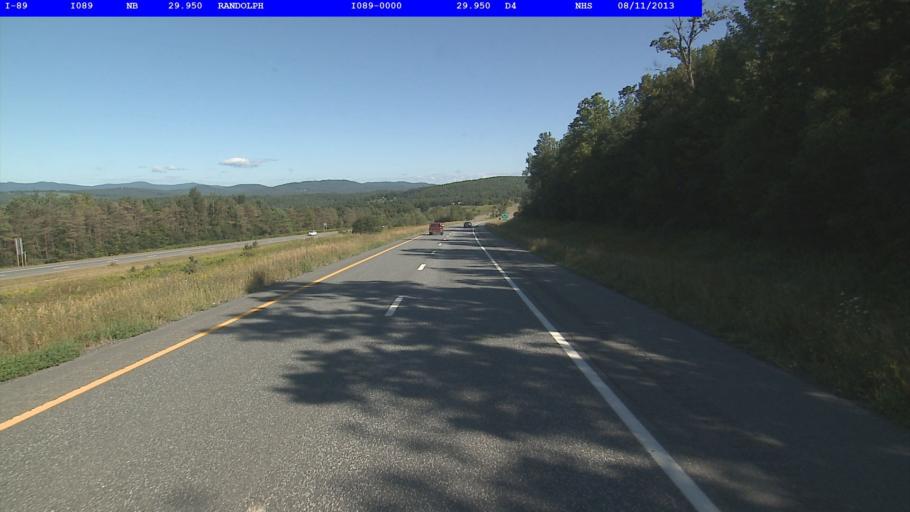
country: US
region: Vermont
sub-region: Orange County
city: Randolph
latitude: 43.9311
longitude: -72.6189
